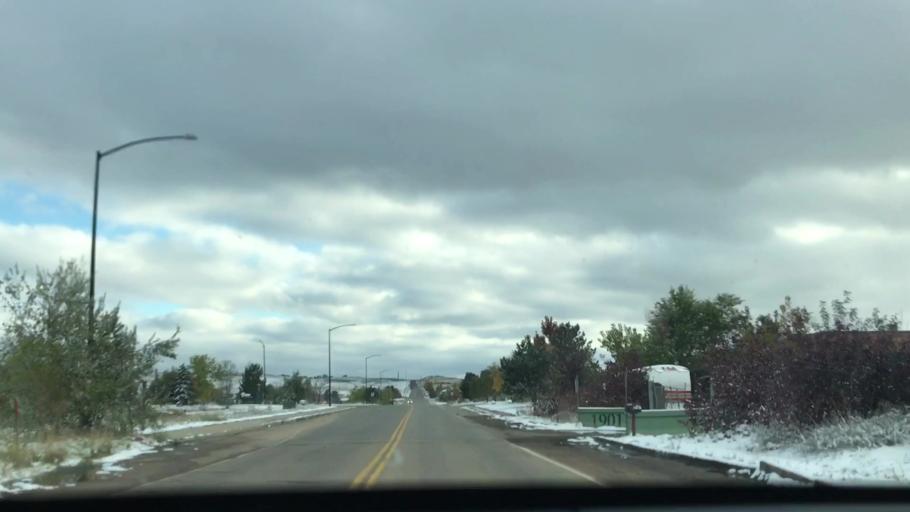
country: US
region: Colorado
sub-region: Boulder County
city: Lafayette
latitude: 39.9814
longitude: -105.0719
